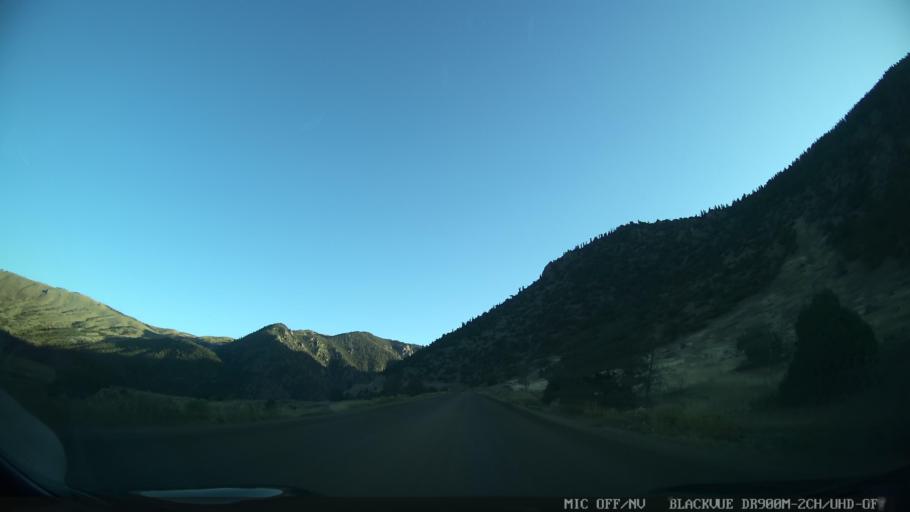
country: US
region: Colorado
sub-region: Grand County
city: Kremmling
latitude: 39.9923
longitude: -106.4910
